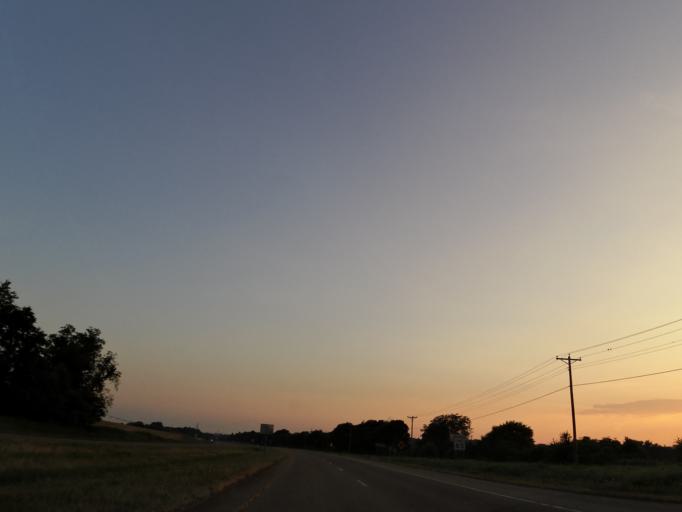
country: US
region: Tennessee
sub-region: Henry County
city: Paris
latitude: 36.2247
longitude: -88.3839
